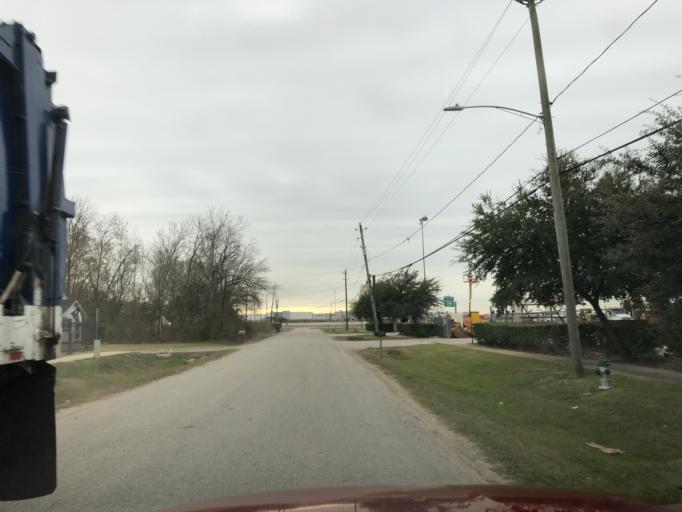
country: US
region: Texas
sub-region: Fort Bend County
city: Missouri City
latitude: 29.6348
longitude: -95.5252
